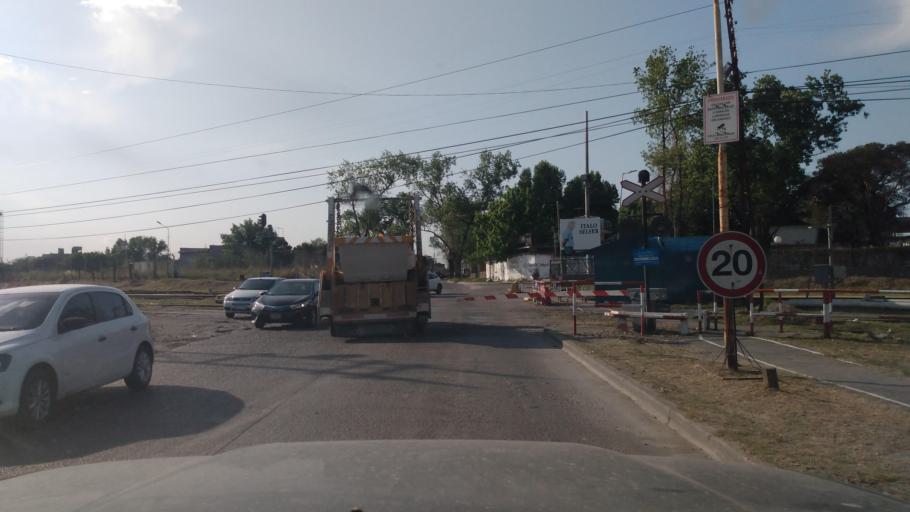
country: AR
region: Buenos Aires
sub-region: Partido de Moron
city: Moron
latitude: -34.6465
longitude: -58.6095
